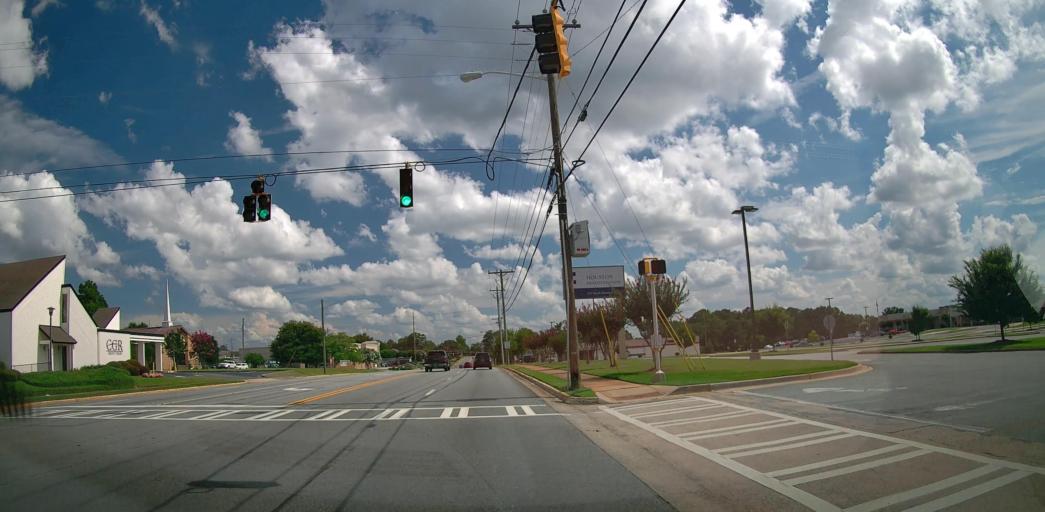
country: US
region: Georgia
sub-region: Houston County
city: Warner Robins
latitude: 32.6205
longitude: -83.6416
